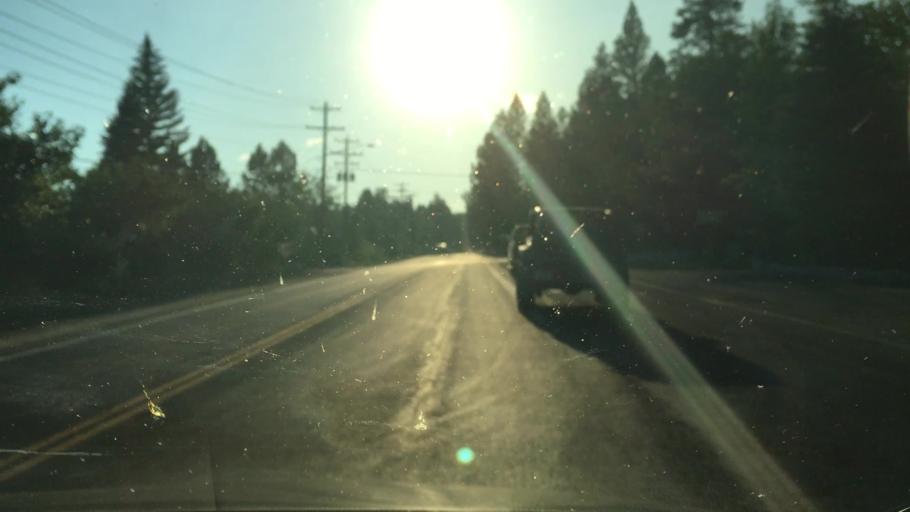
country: US
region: Idaho
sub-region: Valley County
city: McCall
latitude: 44.9126
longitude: -116.1218
